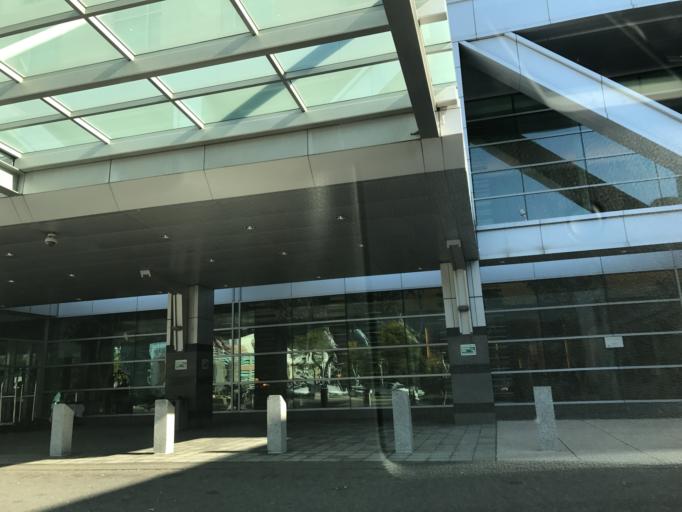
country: US
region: Massachusetts
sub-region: Suffolk County
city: South Boston
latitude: 42.3458
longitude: -71.0439
